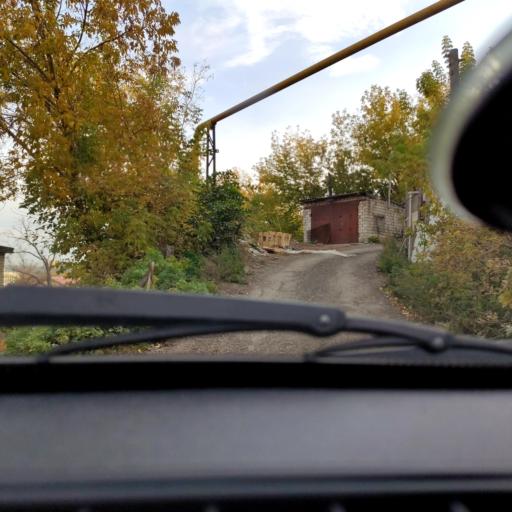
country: RU
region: Bashkortostan
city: Ufa
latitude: 54.7445
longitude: 55.9408
